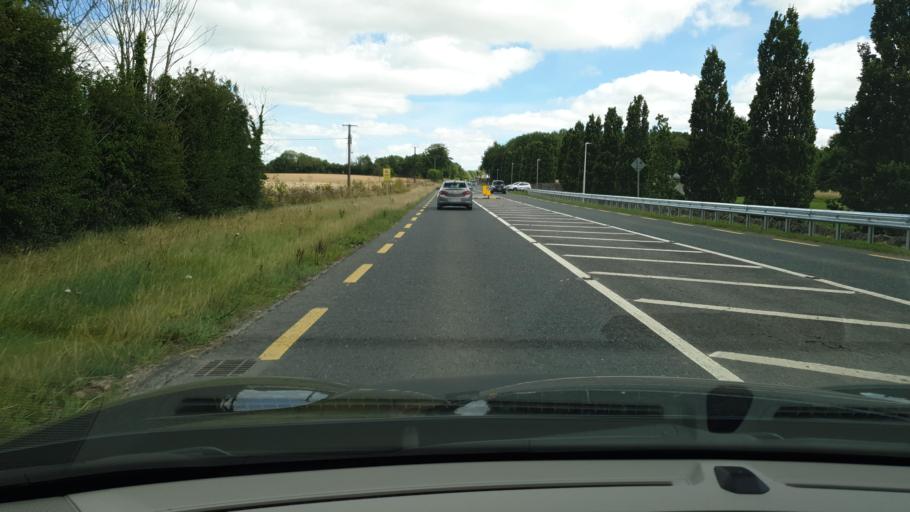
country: IE
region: Leinster
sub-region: An Mhi
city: Newtown Trim
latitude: 53.5249
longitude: -6.6665
